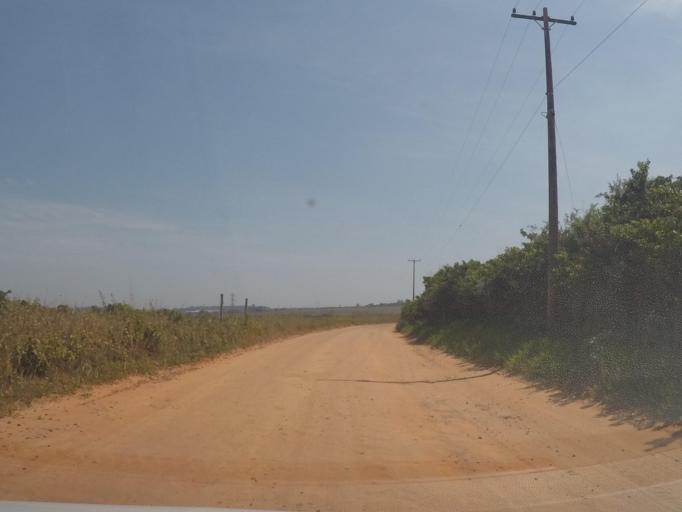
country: BR
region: Sao Paulo
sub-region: Sumare
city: Sumare
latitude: -22.8626
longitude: -47.2780
